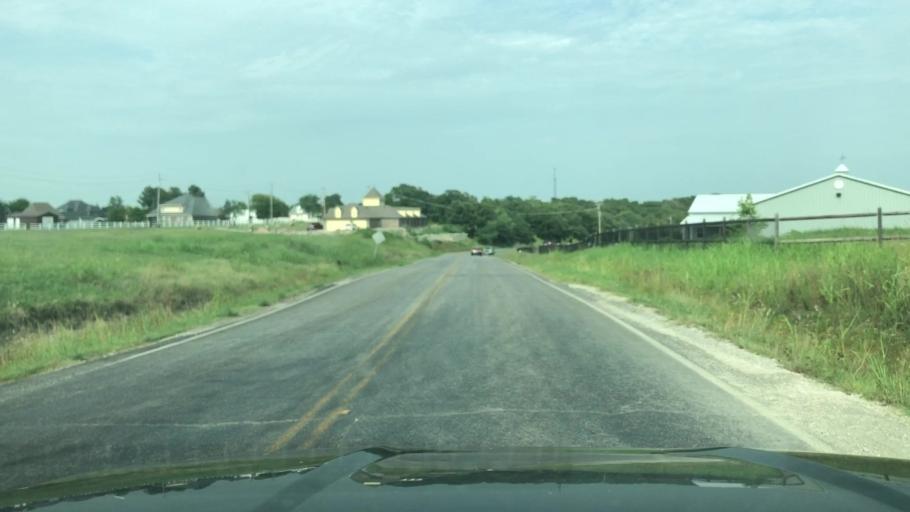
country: US
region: Oklahoma
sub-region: Tulsa County
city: Oakhurst
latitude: 36.0903
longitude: -96.0857
